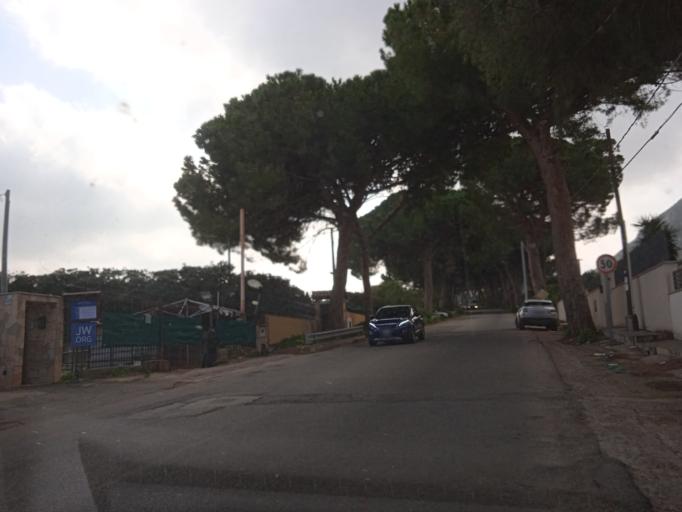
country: IT
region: Sicily
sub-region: Palermo
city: Portella di Mare
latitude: 38.0671
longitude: 13.4588
